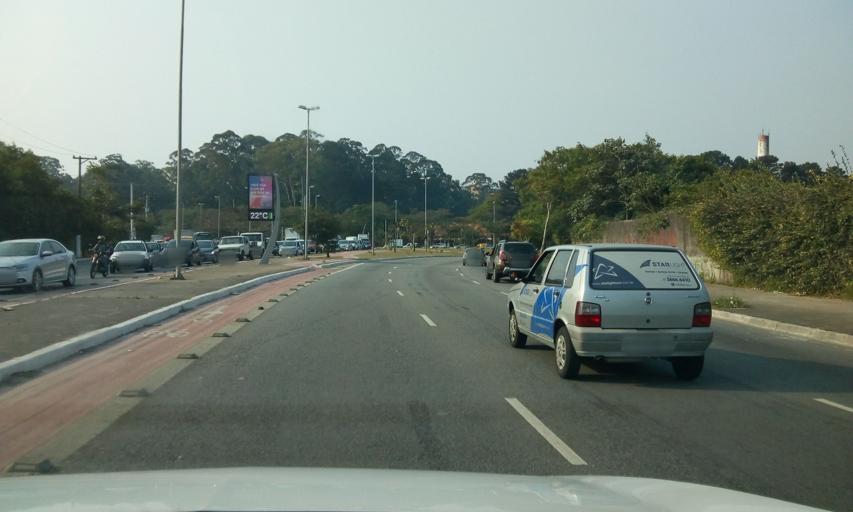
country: BR
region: Sao Paulo
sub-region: Diadema
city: Diadema
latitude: -23.6958
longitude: -46.6837
